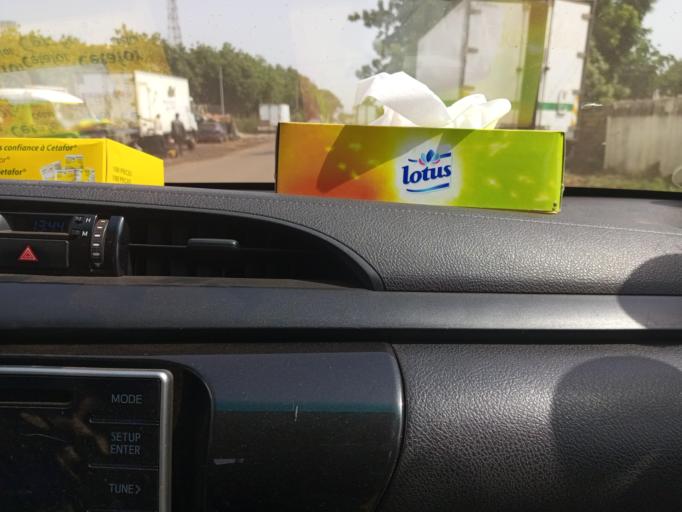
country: ML
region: Bamako
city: Bamako
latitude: 12.6598
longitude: -7.9952
